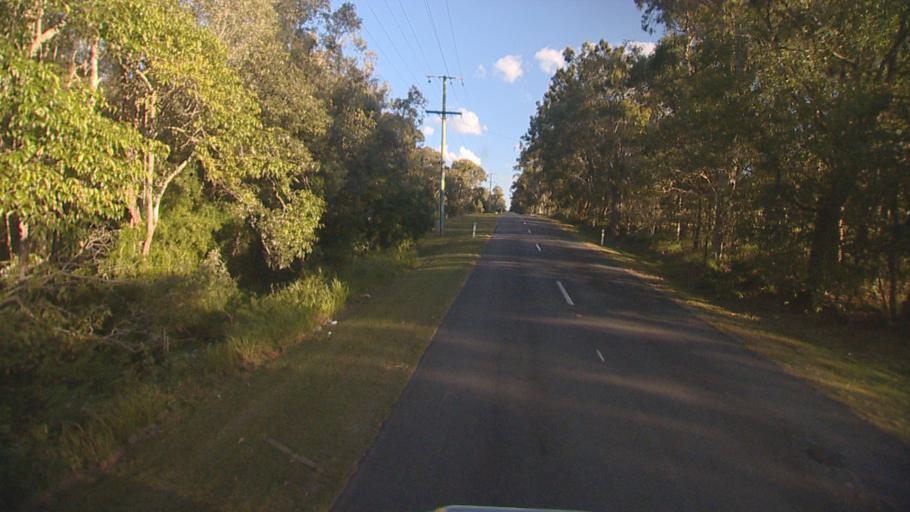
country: AU
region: Queensland
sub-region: Redland
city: Redland Bay
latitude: -27.6740
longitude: 153.2764
